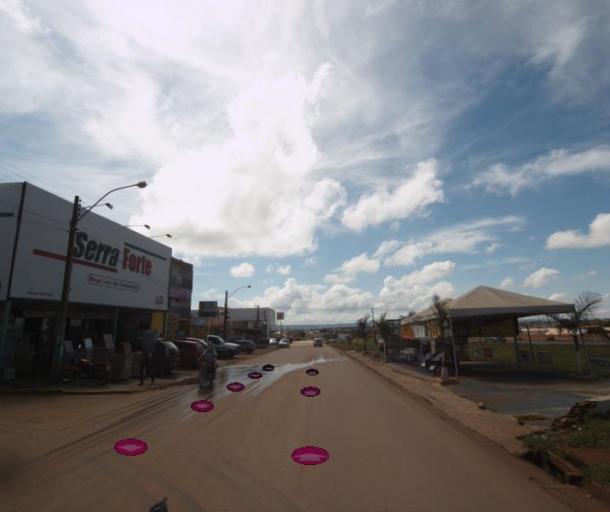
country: BR
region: Federal District
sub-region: Brasilia
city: Brasilia
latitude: -15.7353
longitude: -48.2821
